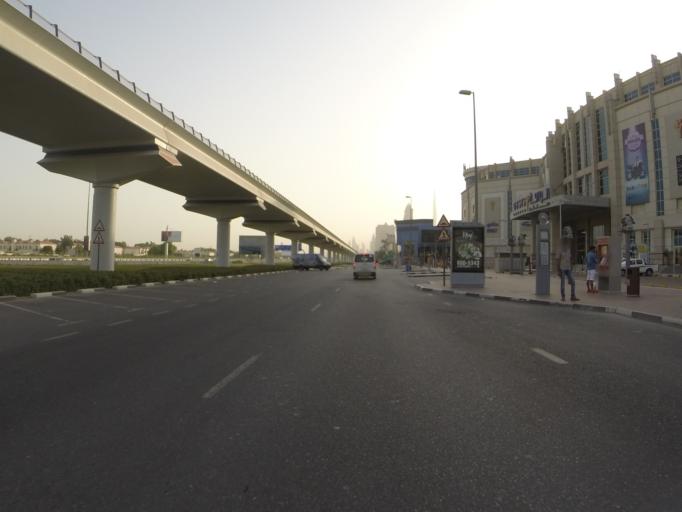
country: AE
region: Dubai
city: Dubai
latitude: 25.1695
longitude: 55.2406
